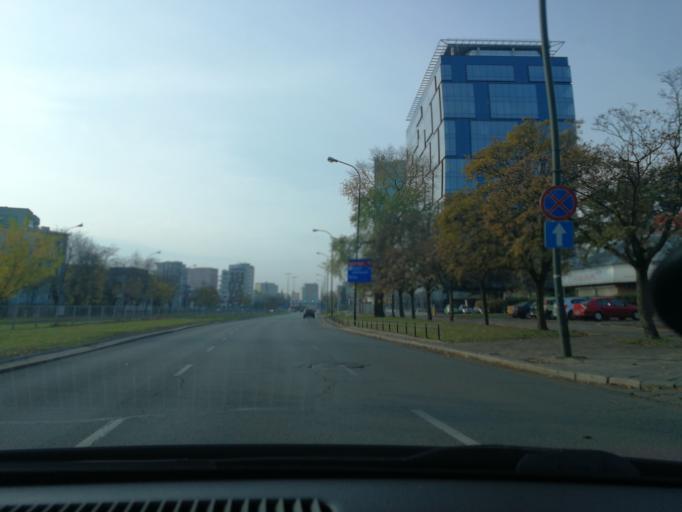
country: PL
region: Masovian Voivodeship
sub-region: Warszawa
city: Praga Poludnie
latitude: 52.2430
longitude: 21.0840
